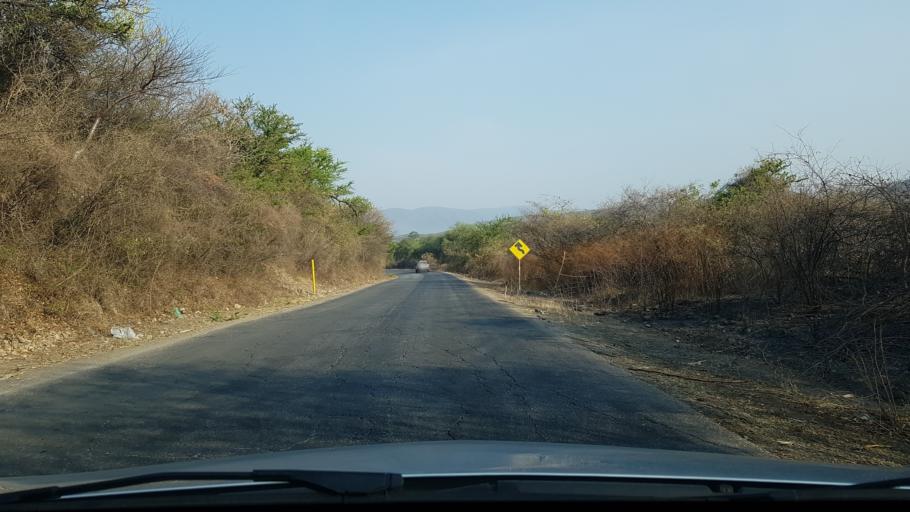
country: MX
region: Morelos
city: Tlaltizapan
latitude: 18.6786
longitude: -99.0871
